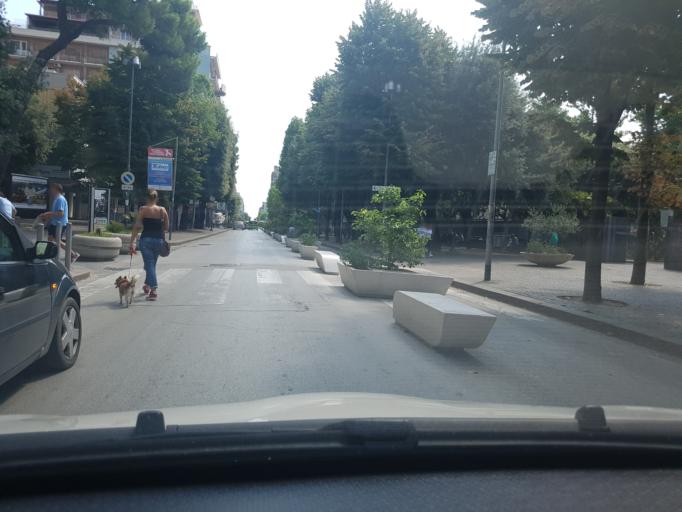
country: IT
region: Apulia
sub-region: Provincia di Foggia
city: Cerignola
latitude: 41.2644
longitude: 15.9035
